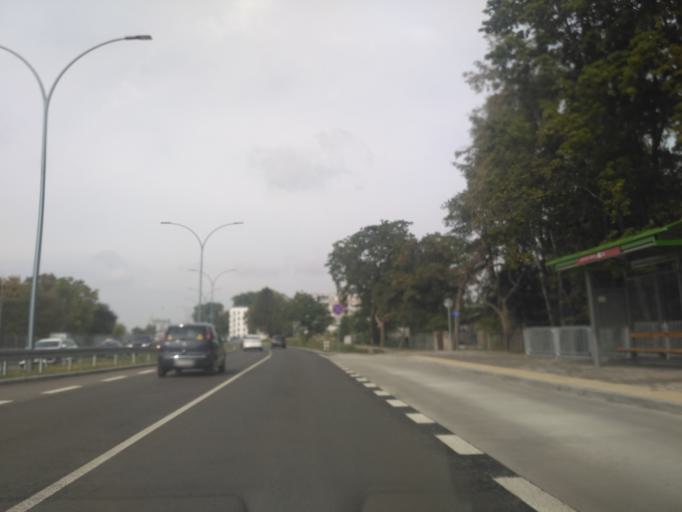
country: PL
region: Lublin Voivodeship
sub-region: Powiat lubelski
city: Lublin
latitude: 51.2234
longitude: 22.5670
